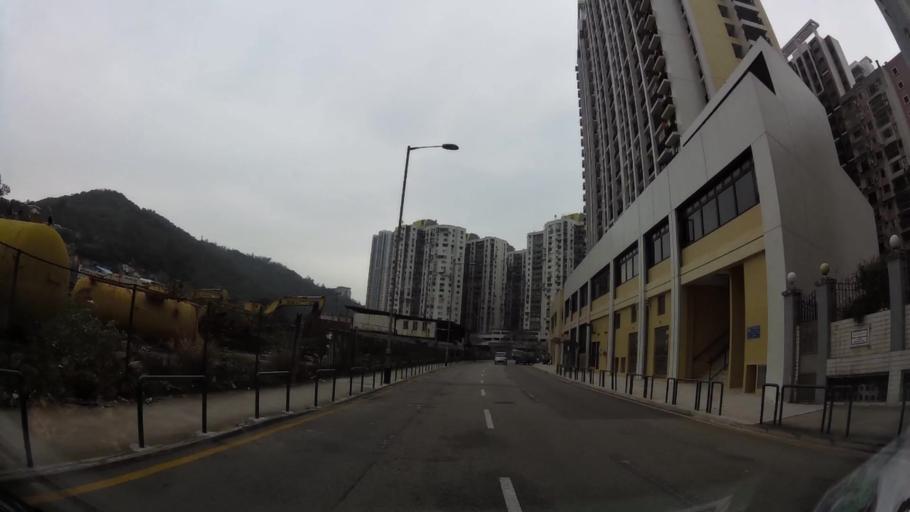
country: MO
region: Macau
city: Macau
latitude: 22.1644
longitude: 113.5610
